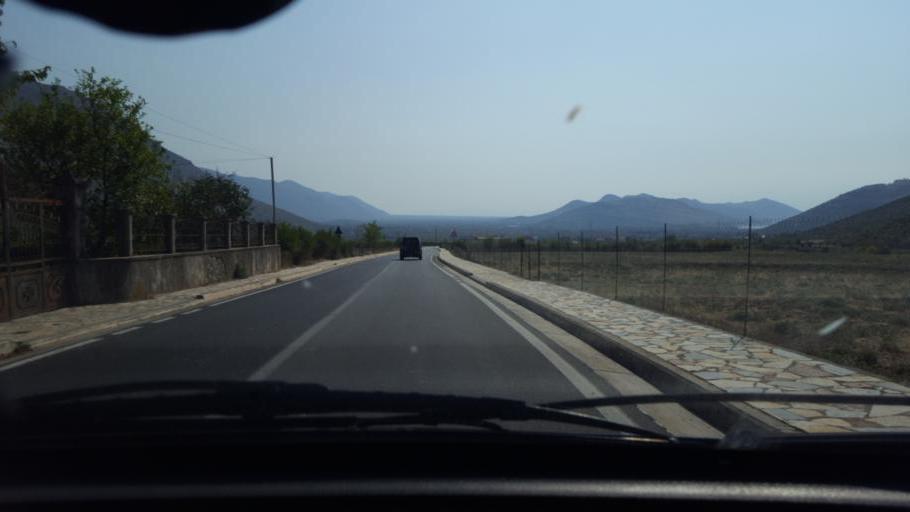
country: AL
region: Shkoder
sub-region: Rrethi i Malesia e Madhe
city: Hot
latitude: 42.3576
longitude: 19.4430
